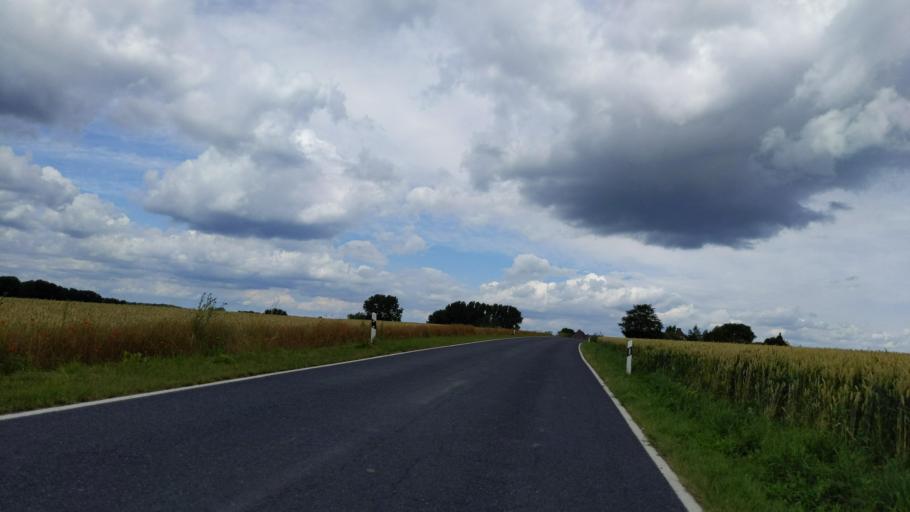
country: DE
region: Mecklenburg-Vorpommern
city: Dassow
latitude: 53.9496
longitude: 10.9736
